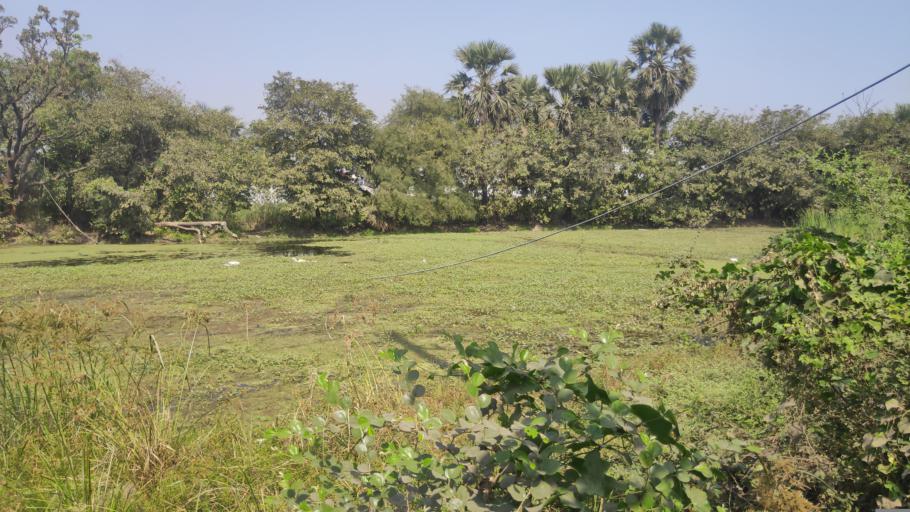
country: IN
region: Maharashtra
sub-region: Thane
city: Kalyan
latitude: 19.2844
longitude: 73.1072
